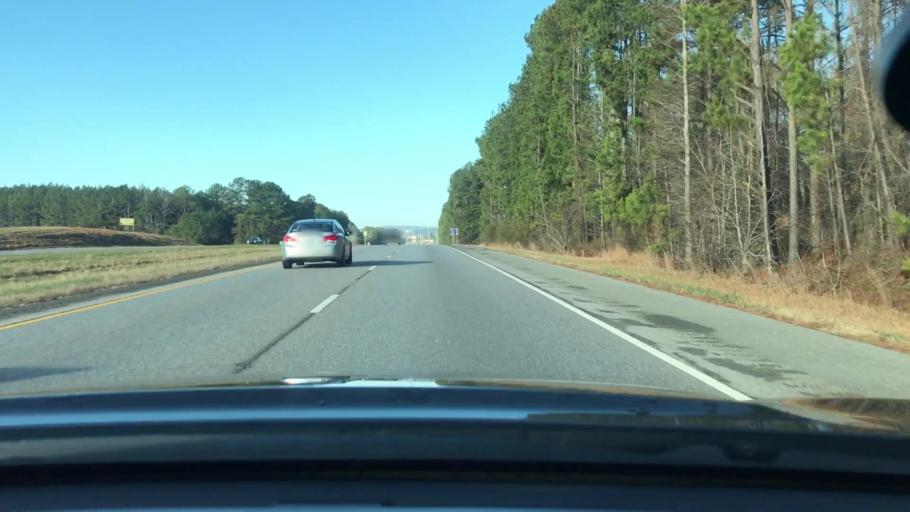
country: US
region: Alabama
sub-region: Shelby County
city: Chelsea
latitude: 33.3508
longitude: -86.5975
